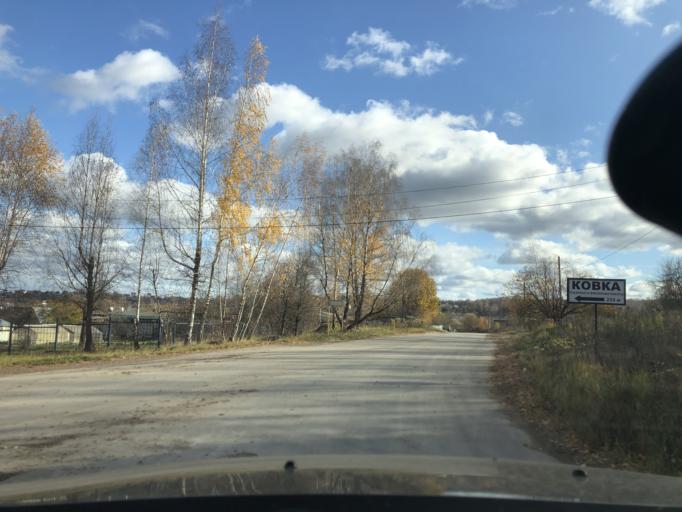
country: RU
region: Tula
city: Gorelki
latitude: 54.2953
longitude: 37.5547
